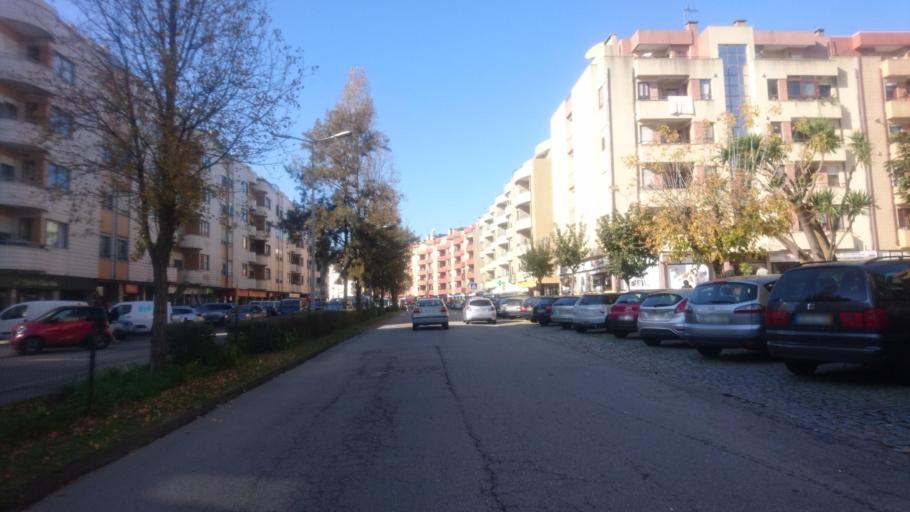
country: PT
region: Aveiro
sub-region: Santa Maria da Feira
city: Feira
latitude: 40.9244
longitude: -8.5617
